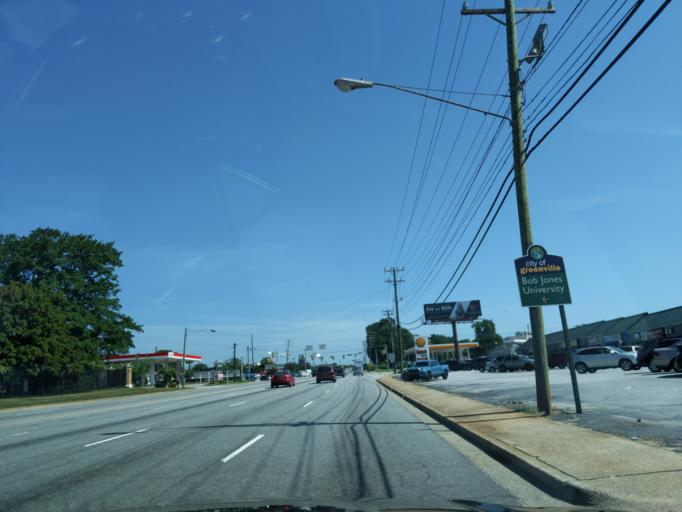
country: US
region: South Carolina
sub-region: Greenville County
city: Wade Hampton
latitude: 34.8769
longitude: -82.3593
